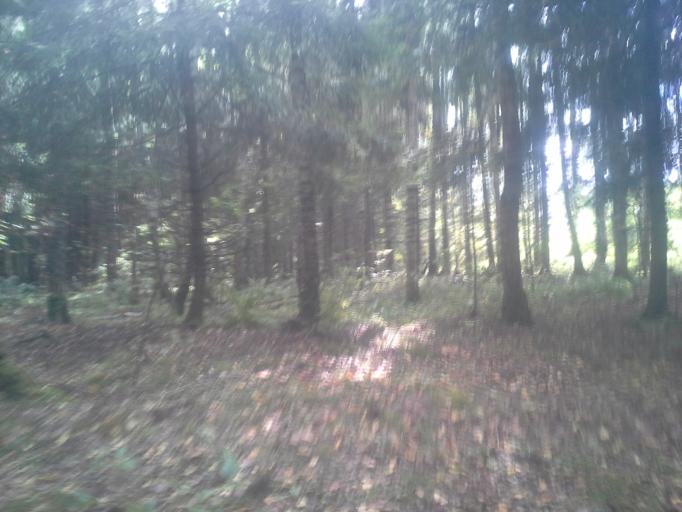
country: RU
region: Moskovskaya
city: Kievskij
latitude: 55.3487
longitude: 36.9589
